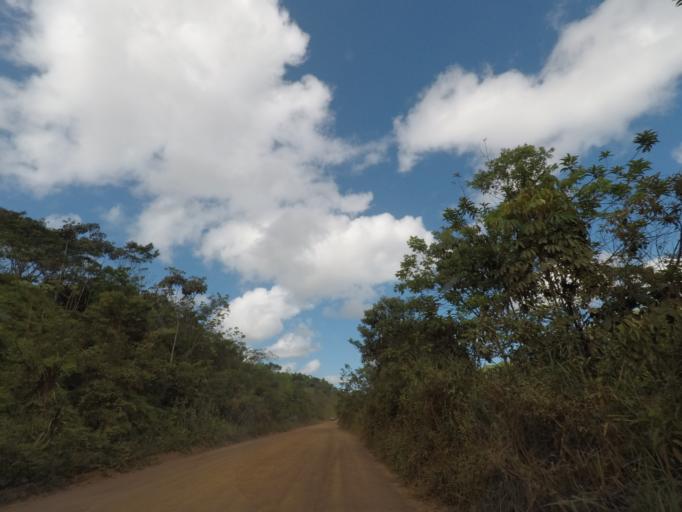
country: BR
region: Bahia
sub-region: Itacare
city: Itacare
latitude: -14.2215
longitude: -39.0765
